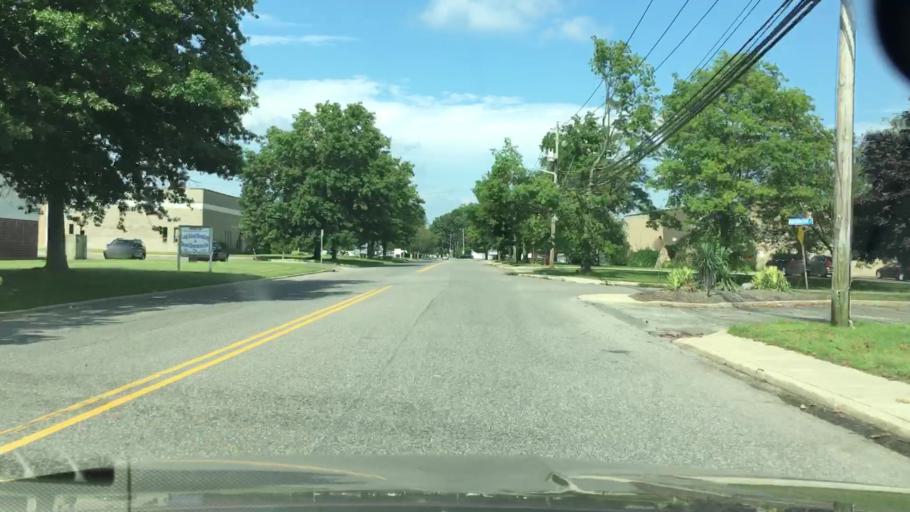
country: US
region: New York
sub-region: Suffolk County
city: Islandia
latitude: 40.7951
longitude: -73.1388
